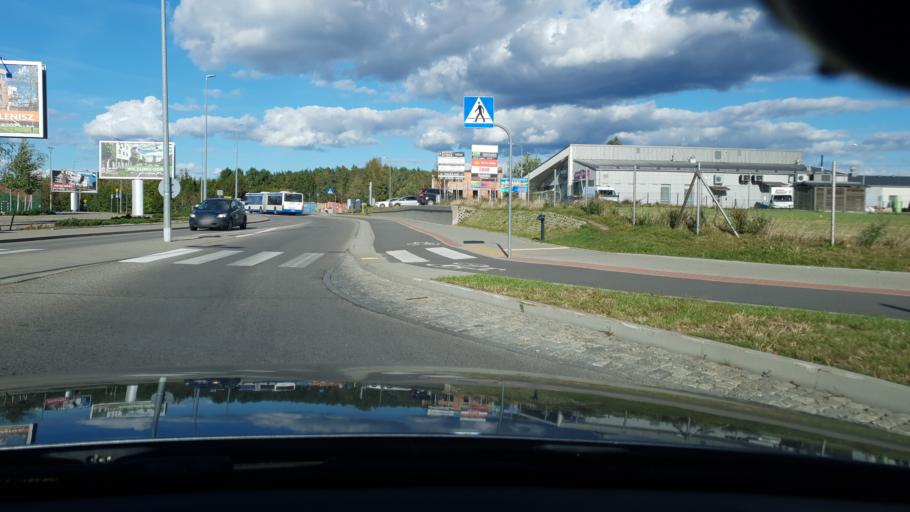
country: PL
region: Pomeranian Voivodeship
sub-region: Powiat kartuski
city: Chwaszczyno
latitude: 54.4967
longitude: 18.4383
